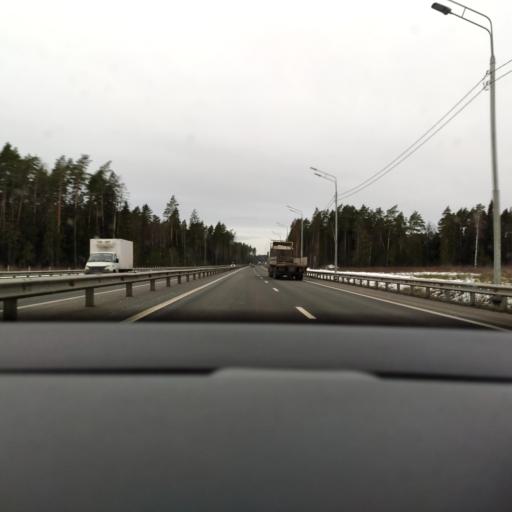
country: RU
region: Moskovskaya
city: Bol'shiye Vyazemy
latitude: 55.6613
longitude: 36.9543
